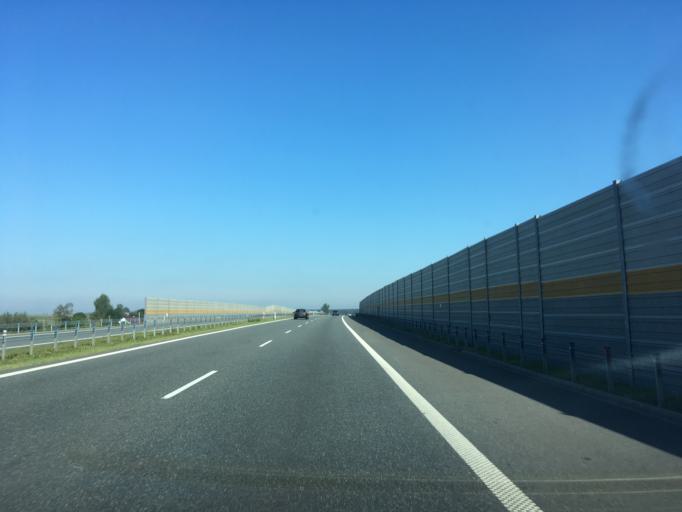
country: PL
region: Kujawsko-Pomorskie
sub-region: Powiat torunski
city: Lubicz Dolny
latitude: 53.1278
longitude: 18.7395
